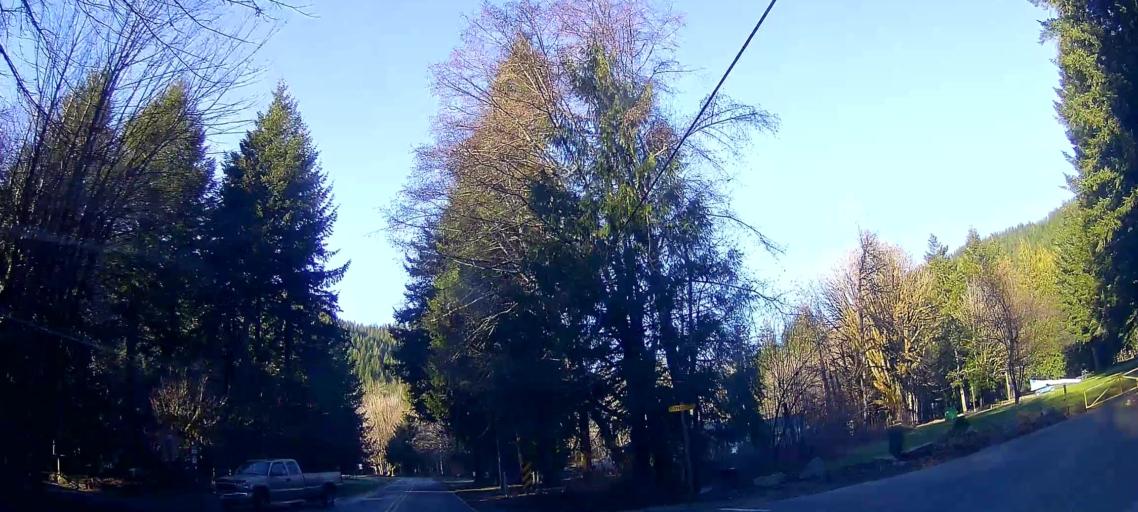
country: US
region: Washington
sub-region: Snohomish County
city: Darrington
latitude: 48.5788
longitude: -121.7740
